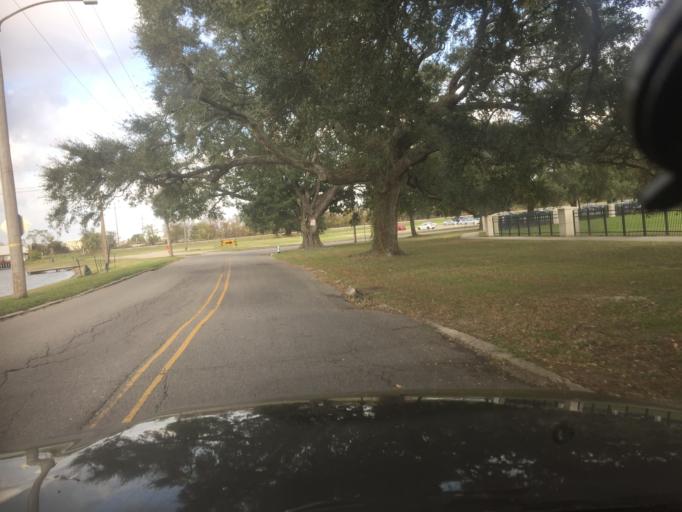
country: US
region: Louisiana
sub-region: Orleans Parish
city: New Orleans
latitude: 29.9912
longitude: -90.0865
